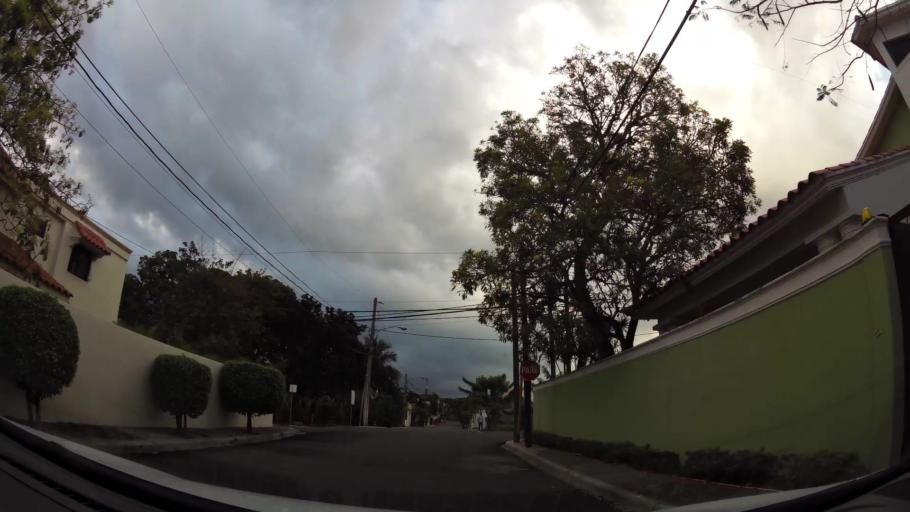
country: DO
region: Nacional
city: Santo Domingo
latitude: 18.5013
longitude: -69.9719
